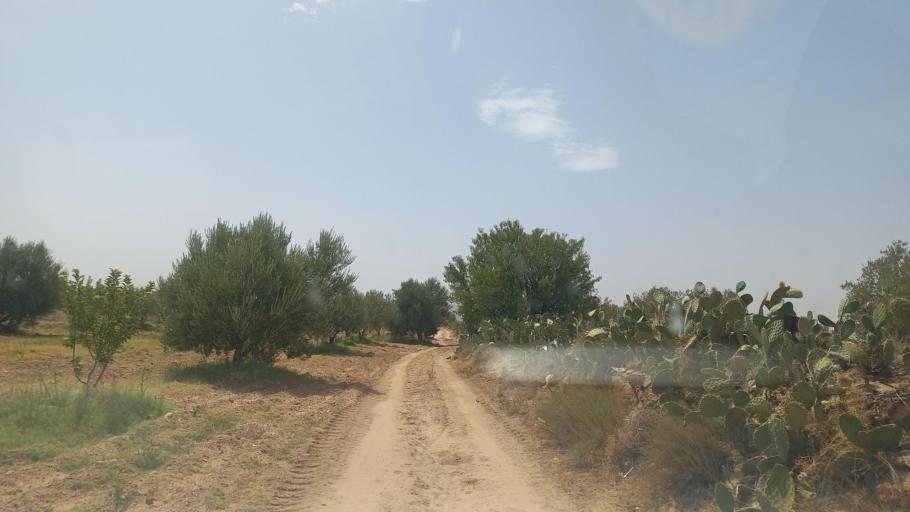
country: TN
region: Al Qasrayn
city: Kasserine
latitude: 35.2612
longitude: 9.0055
